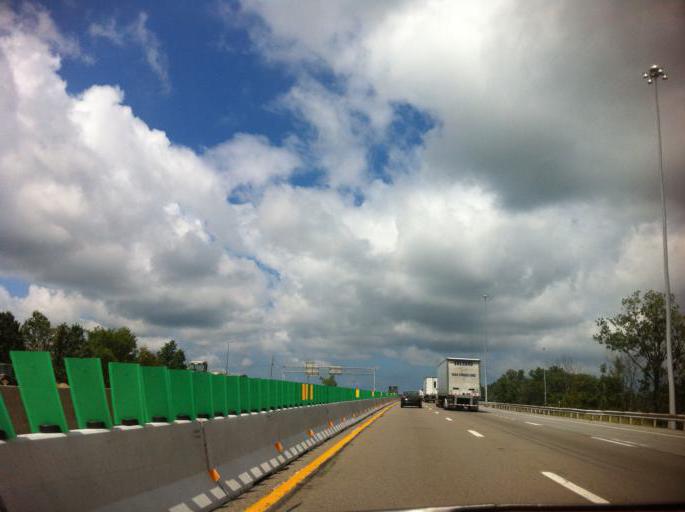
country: US
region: Ohio
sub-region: Lorain County
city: Elyria
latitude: 41.3884
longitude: -82.1135
